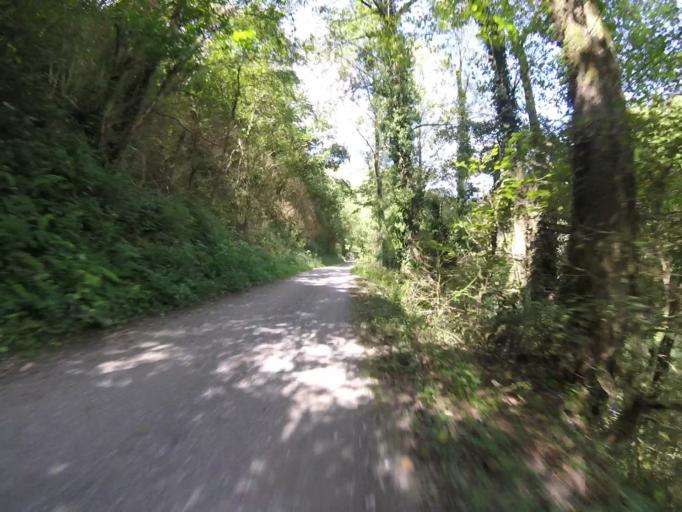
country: ES
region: Navarre
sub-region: Provincia de Navarra
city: Igantzi
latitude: 43.2099
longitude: -1.6688
